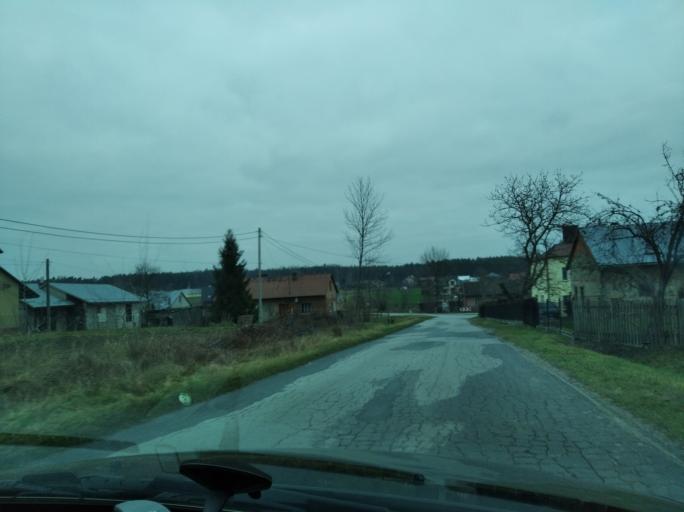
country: PL
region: Subcarpathian Voivodeship
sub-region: Powiat lancucki
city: Brzoza Stadnicka
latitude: 50.1905
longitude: 22.2568
